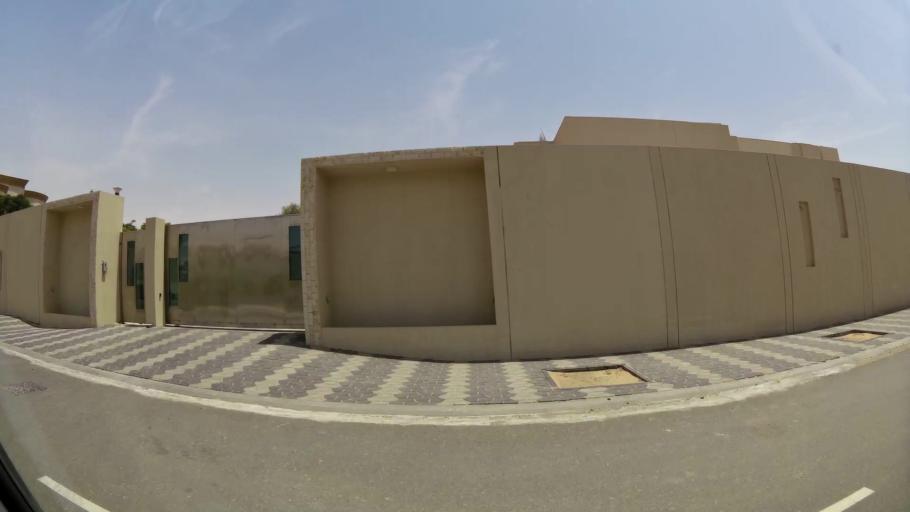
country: AE
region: Ash Shariqah
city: Sharjah
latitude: 25.2375
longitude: 55.4862
